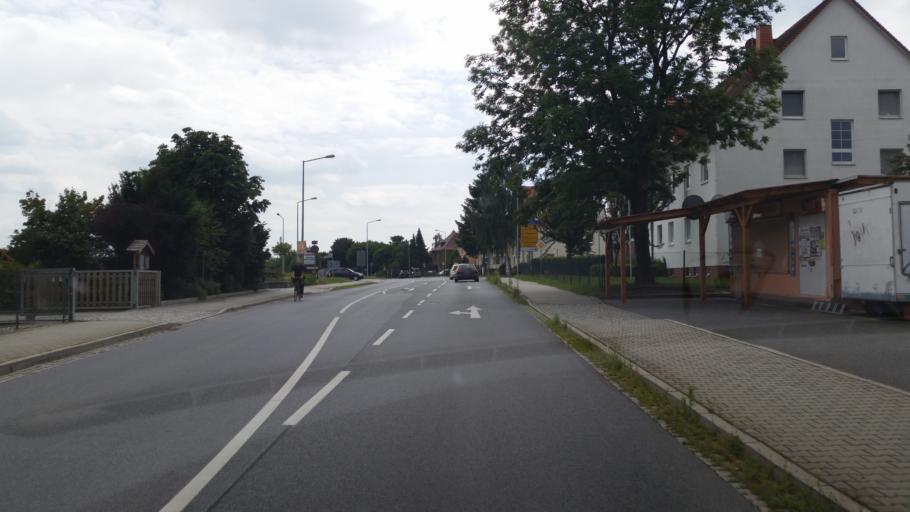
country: DE
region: Saxony
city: Radibor
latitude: 51.2117
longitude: 14.3949
